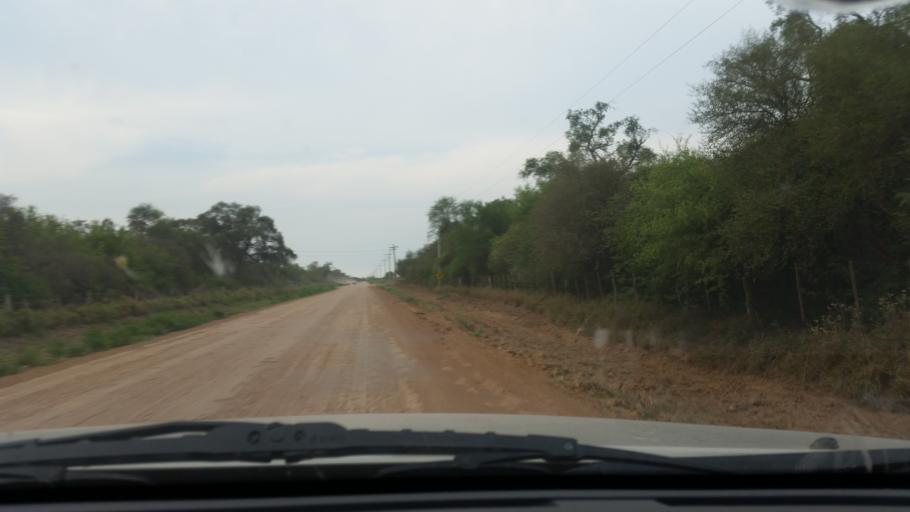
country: PY
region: Boqueron
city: Colonia Menno
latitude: -22.3505
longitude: -59.6229
